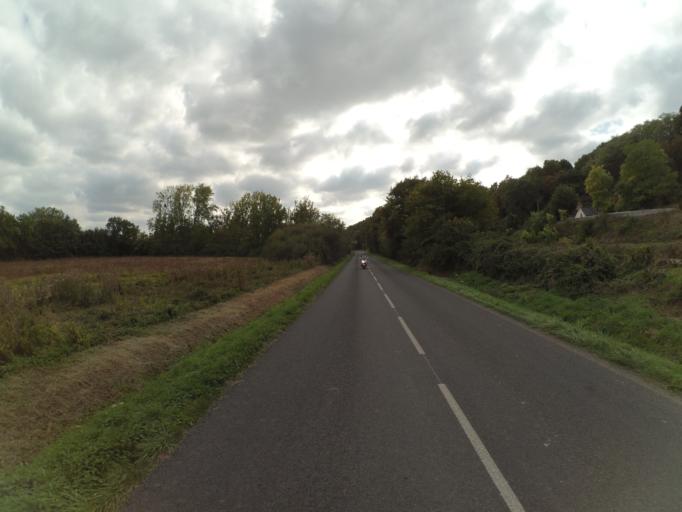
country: FR
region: Centre
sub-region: Departement d'Indre-et-Loire
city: Reugny
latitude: 47.4689
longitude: 0.8800
